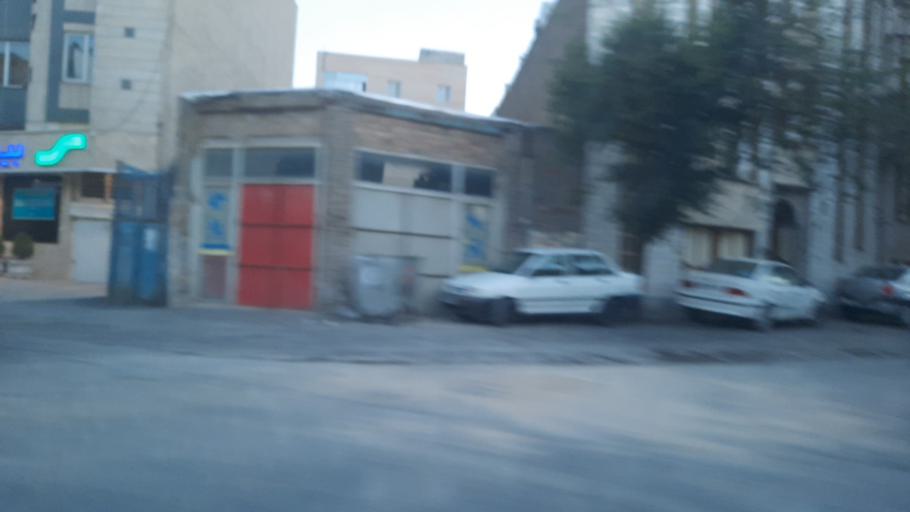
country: IR
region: Markazi
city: Arak
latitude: 34.0760
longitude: 49.6993
